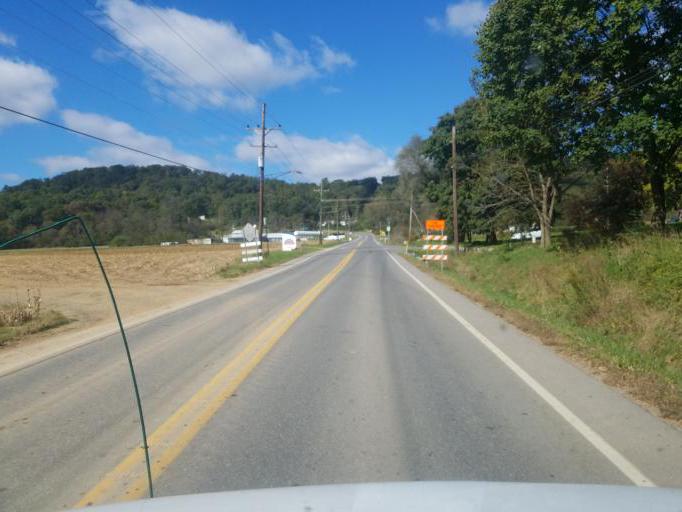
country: US
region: Pennsylvania
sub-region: Fulton County
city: McConnellsburg
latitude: 39.9358
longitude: -78.0085
